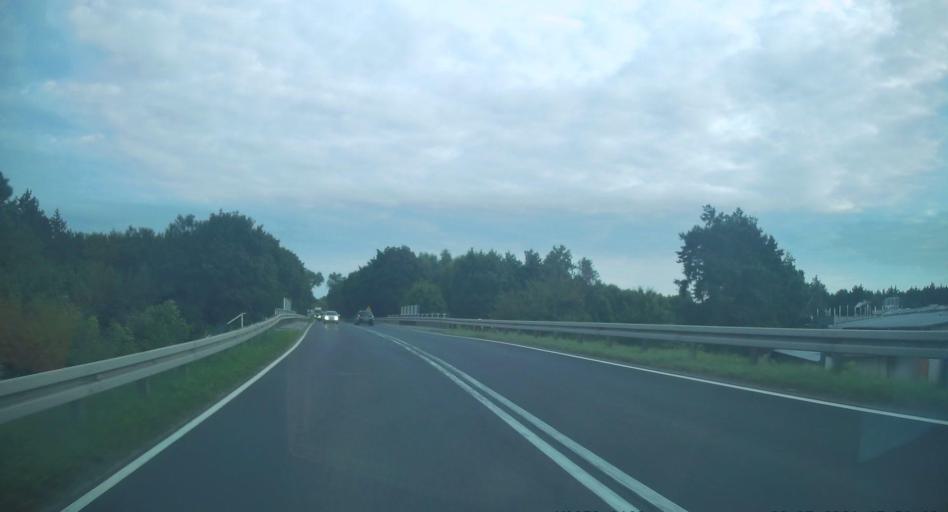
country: PL
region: Lodz Voivodeship
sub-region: Powiat radomszczanski
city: Gomunice
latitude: 51.1846
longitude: 19.4947
